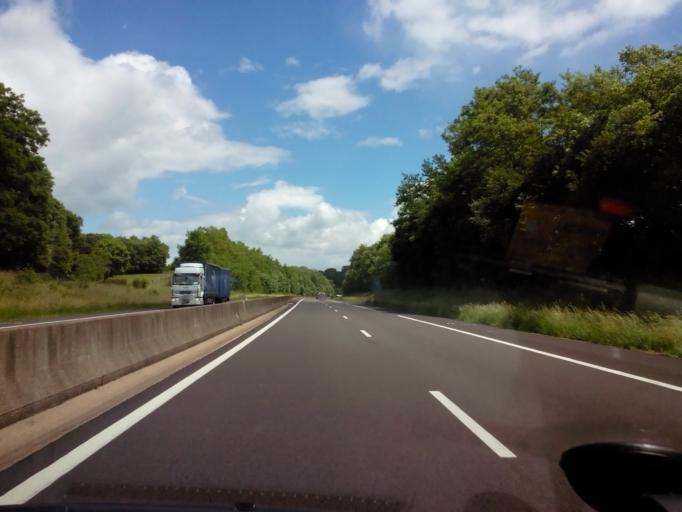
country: FR
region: Champagne-Ardenne
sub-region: Departement de la Haute-Marne
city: Avrecourt
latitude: 47.9556
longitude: 5.4428
